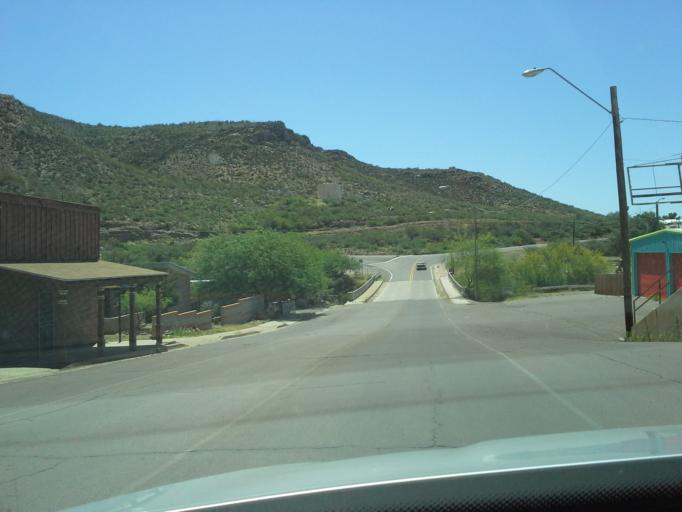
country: US
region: Arizona
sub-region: Pinal County
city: Superior
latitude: 33.2936
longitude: -111.0963
